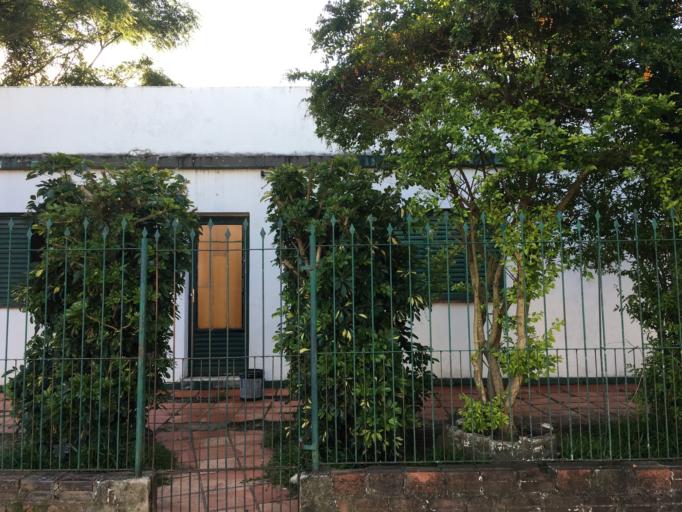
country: BR
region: Rio Grande do Sul
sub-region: Santa Maria
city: Santa Maria
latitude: -29.7010
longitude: -53.7077
